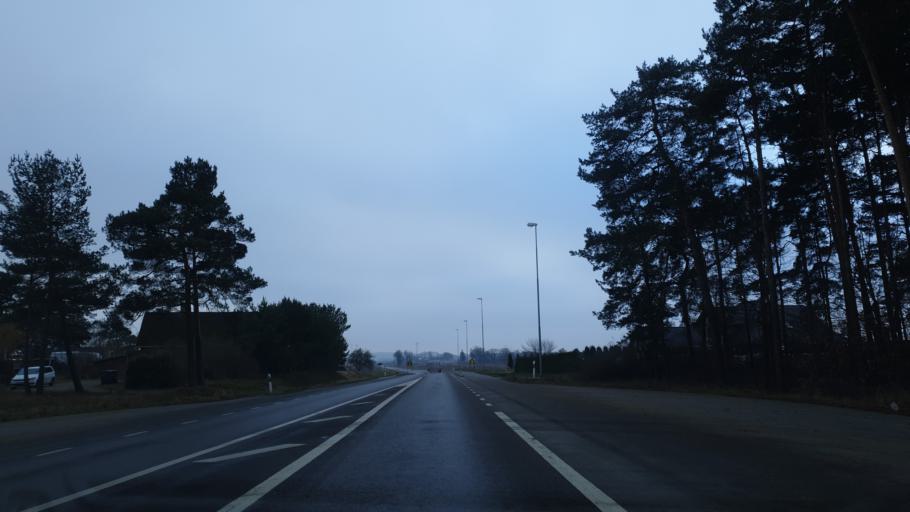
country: SE
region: Blekinge
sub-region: Solvesborgs Kommun
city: Soelvesborg
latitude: 56.0858
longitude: 14.6476
